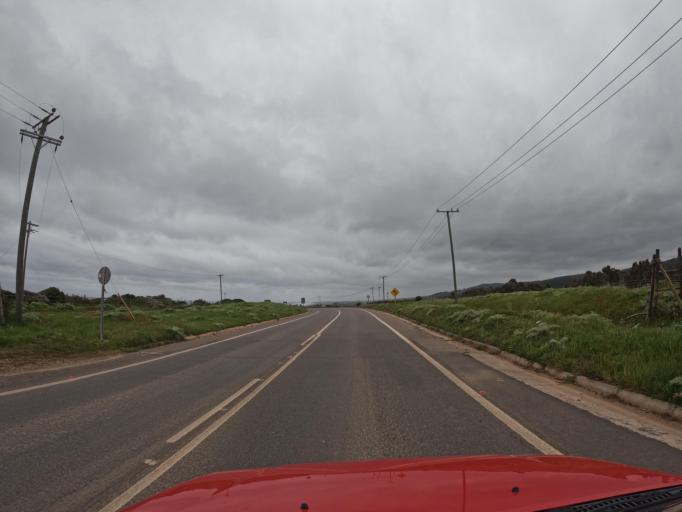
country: CL
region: O'Higgins
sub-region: Provincia de Colchagua
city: Santa Cruz
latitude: -34.4918
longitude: -72.0146
